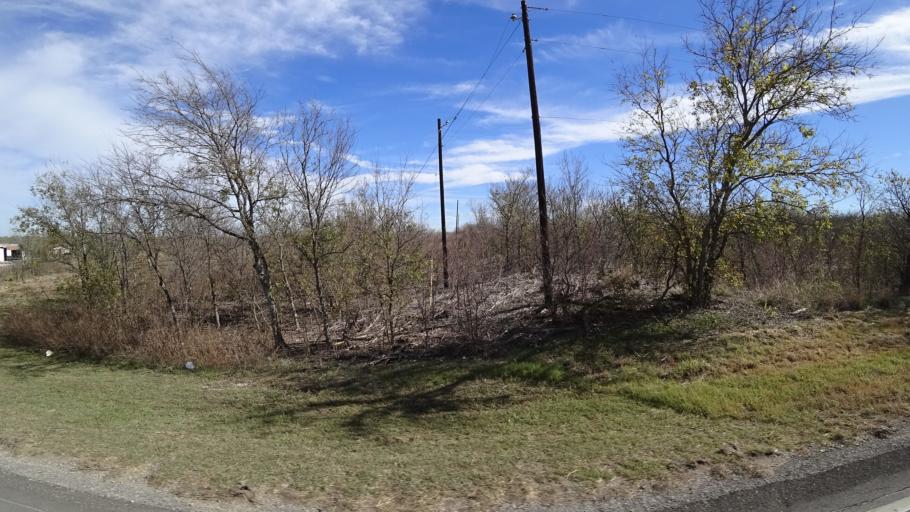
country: US
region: Texas
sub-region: Travis County
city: Onion Creek
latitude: 30.0996
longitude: -97.6942
